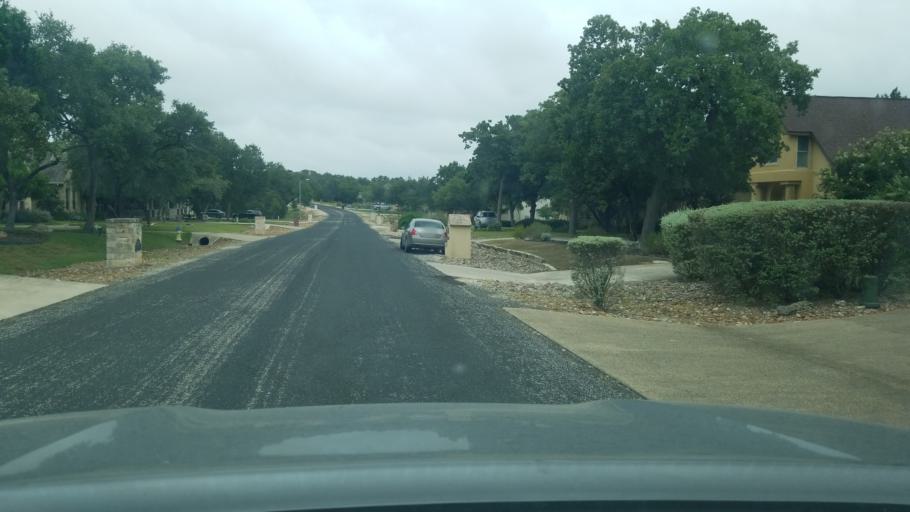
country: US
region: Texas
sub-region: Bexar County
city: Timberwood Park
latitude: 29.7003
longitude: -98.5104
